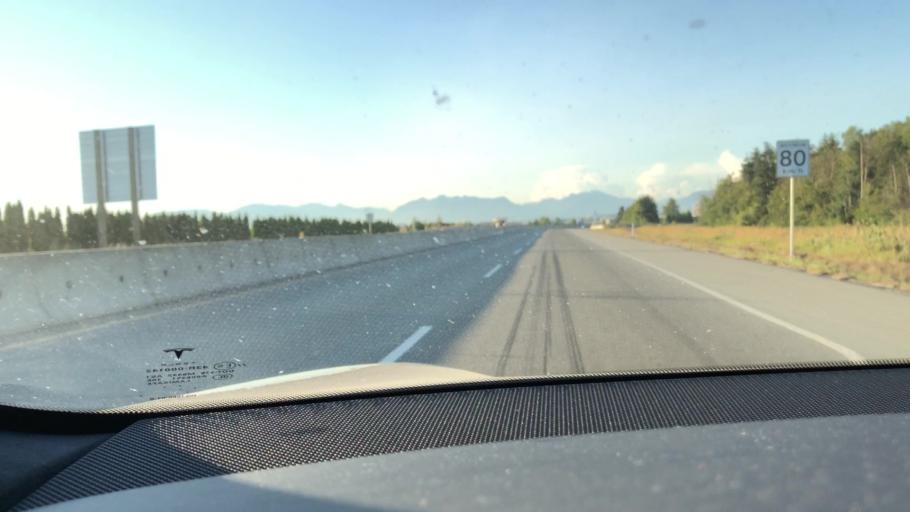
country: CA
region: British Columbia
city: Ladner
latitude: 49.1140
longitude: -123.0289
